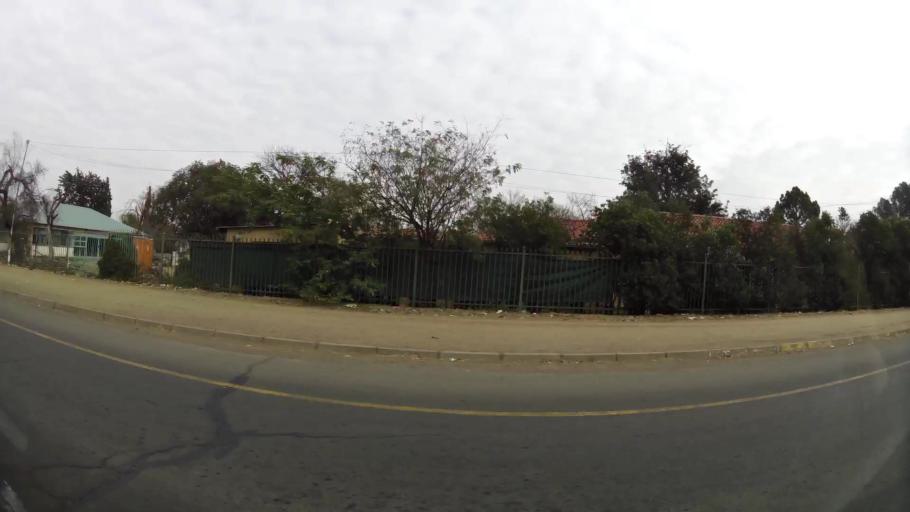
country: ZA
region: Orange Free State
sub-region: Mangaung Metropolitan Municipality
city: Bloemfontein
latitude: -29.1276
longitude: 26.2083
